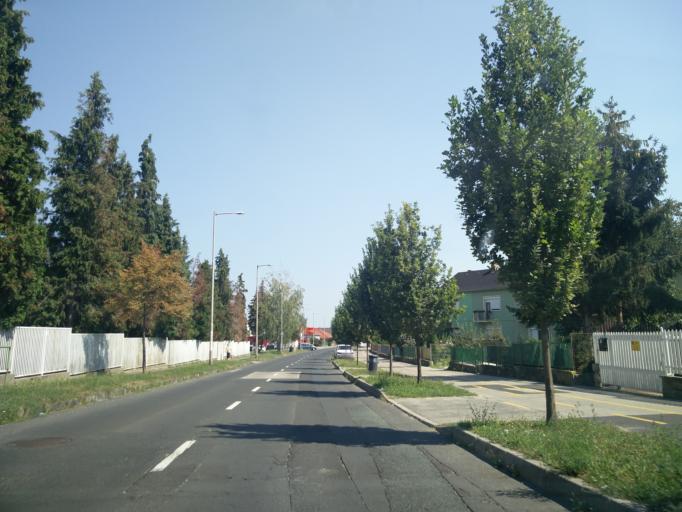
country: HU
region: Zala
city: Zalaegerszeg
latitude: 46.8301
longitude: 16.8350
